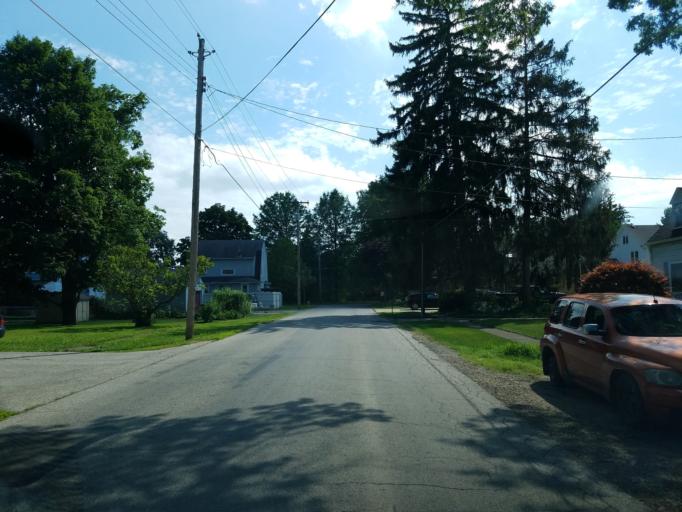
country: US
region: Ohio
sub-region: Ashland County
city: Ashland
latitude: 40.8767
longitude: -82.3297
